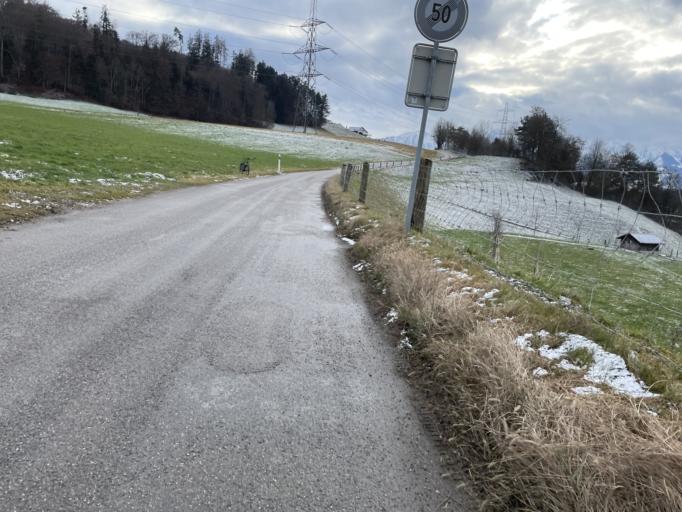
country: CH
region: Lucerne
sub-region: Entlebuch District
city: Oberdiessbach
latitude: 46.8296
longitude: 7.6167
